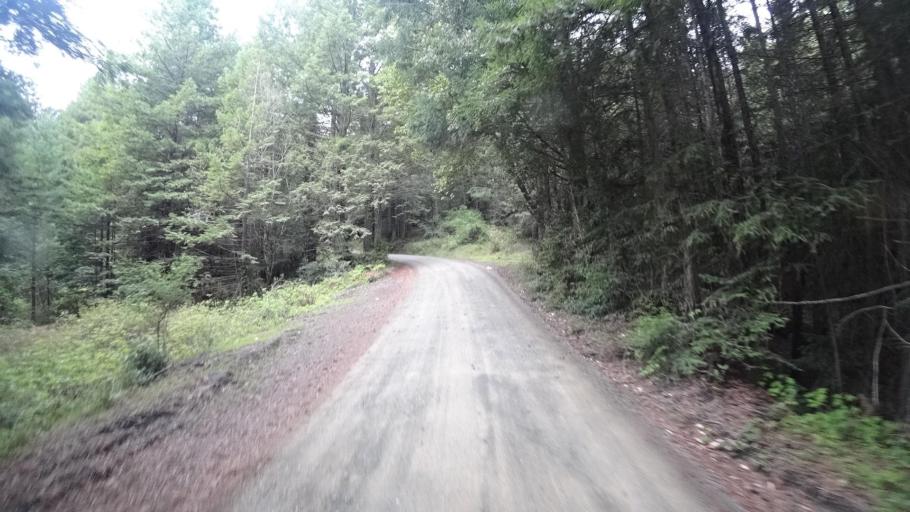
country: US
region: California
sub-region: Humboldt County
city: Redway
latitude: 40.3184
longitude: -123.8296
